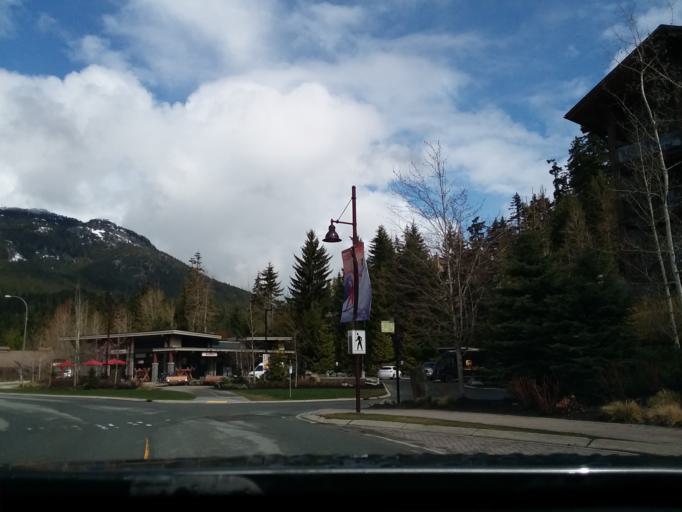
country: CA
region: British Columbia
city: Whistler
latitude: 50.0959
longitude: -122.9894
